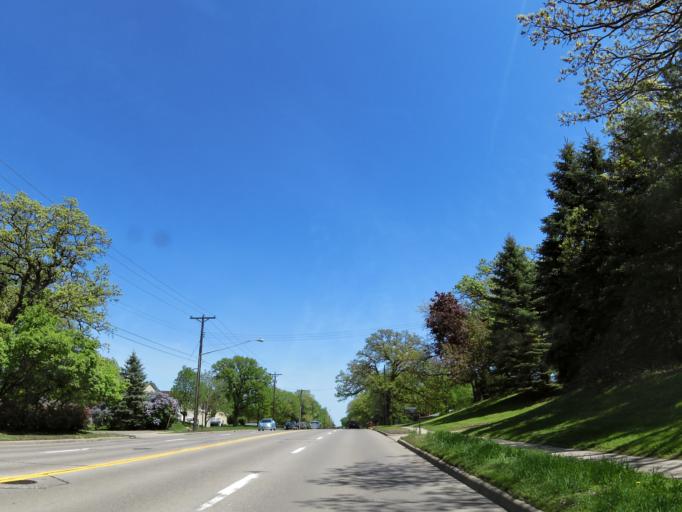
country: US
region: Minnesota
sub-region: Scott County
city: Savage
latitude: 44.8082
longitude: -93.3434
